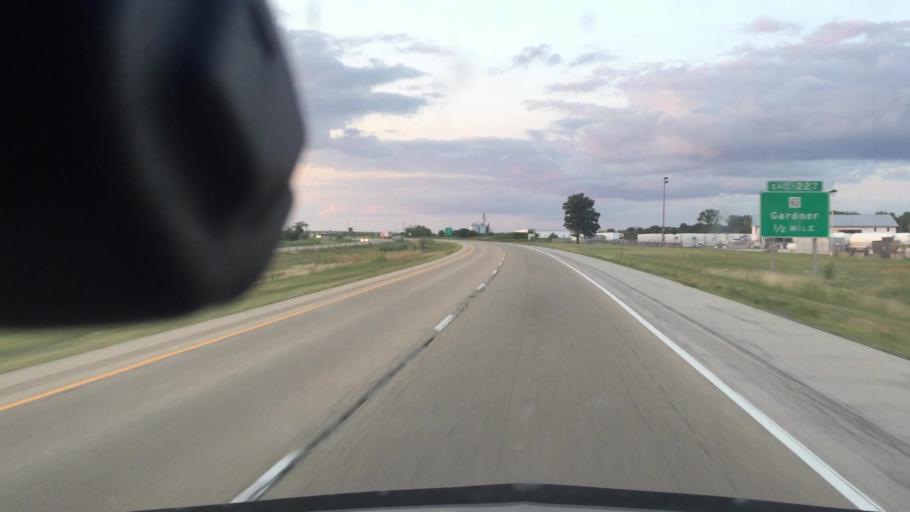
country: US
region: Illinois
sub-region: Grundy County
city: Gardner
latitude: 41.1761
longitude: -88.3250
